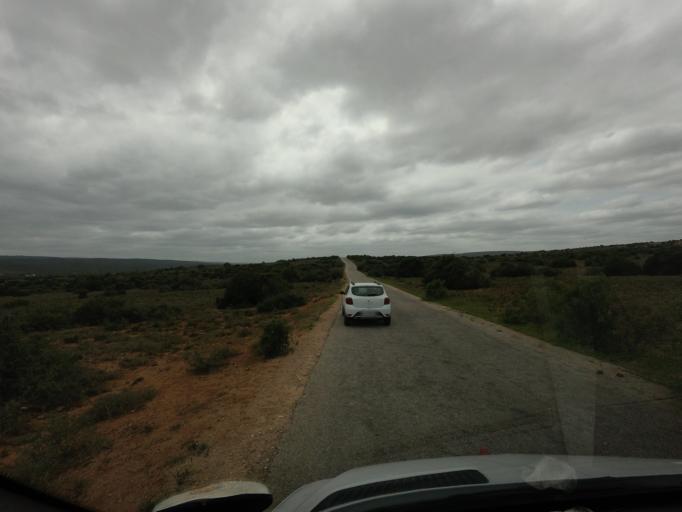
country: ZA
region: Eastern Cape
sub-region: Cacadu District Municipality
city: Kirkwood
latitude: -33.4390
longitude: 25.7781
